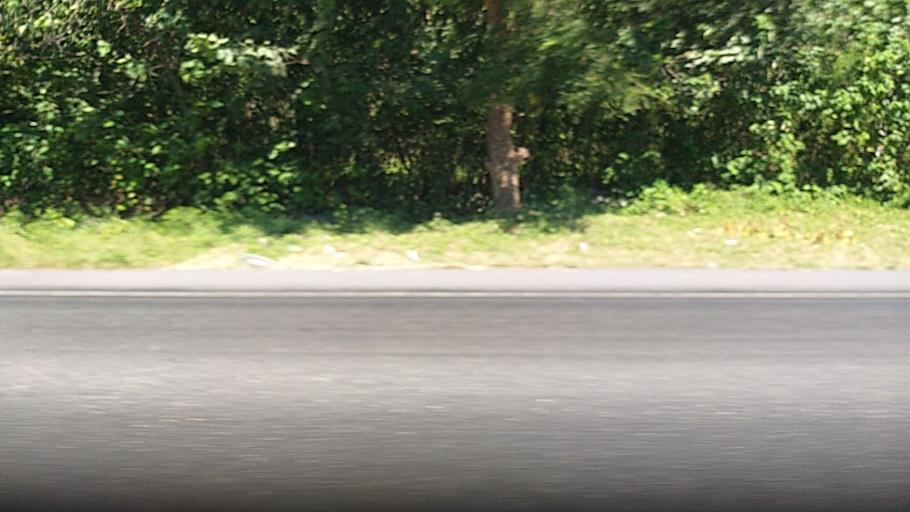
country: TH
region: Sara Buri
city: Muak Lek
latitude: 14.6376
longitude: 101.1528
